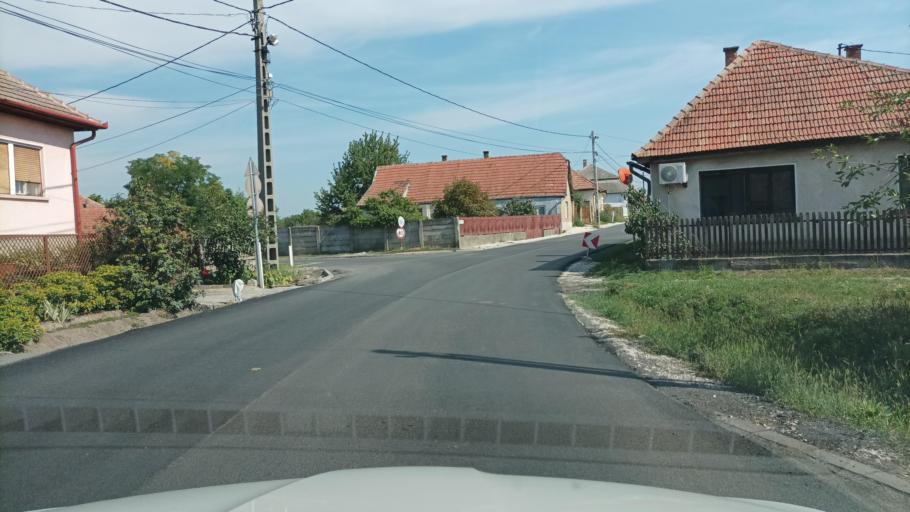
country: HU
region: Pest
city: Tura
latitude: 47.6066
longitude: 19.5967
